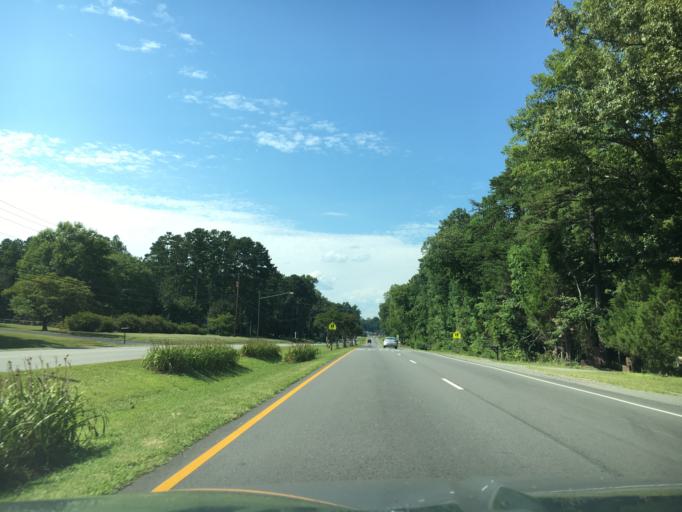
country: US
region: Virginia
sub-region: Halifax County
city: South Boston
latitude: 36.7214
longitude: -78.9180
